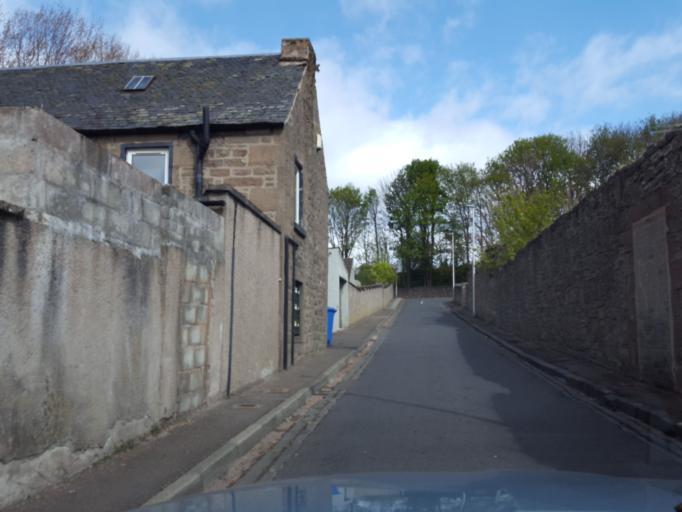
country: GB
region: Scotland
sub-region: Dundee City
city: Dundee
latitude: 56.4747
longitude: -3.0204
